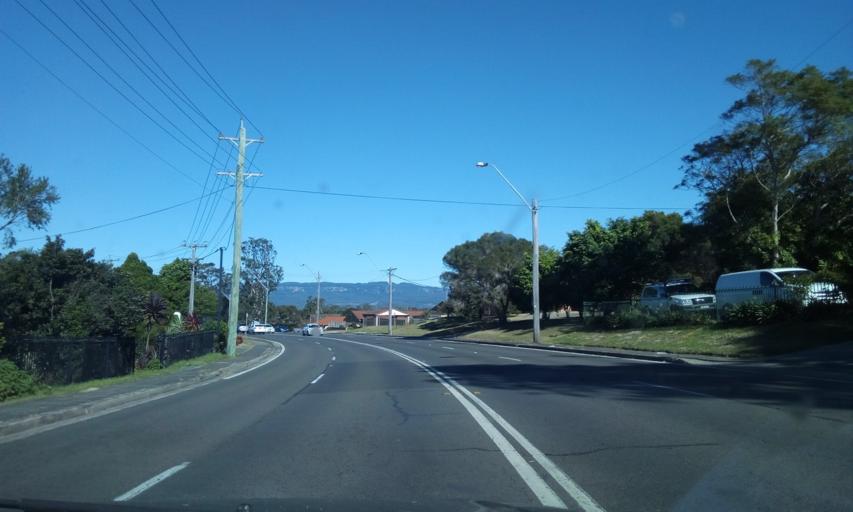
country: AU
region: New South Wales
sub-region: Wollongong
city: Dapto
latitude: -34.5112
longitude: 150.7854
